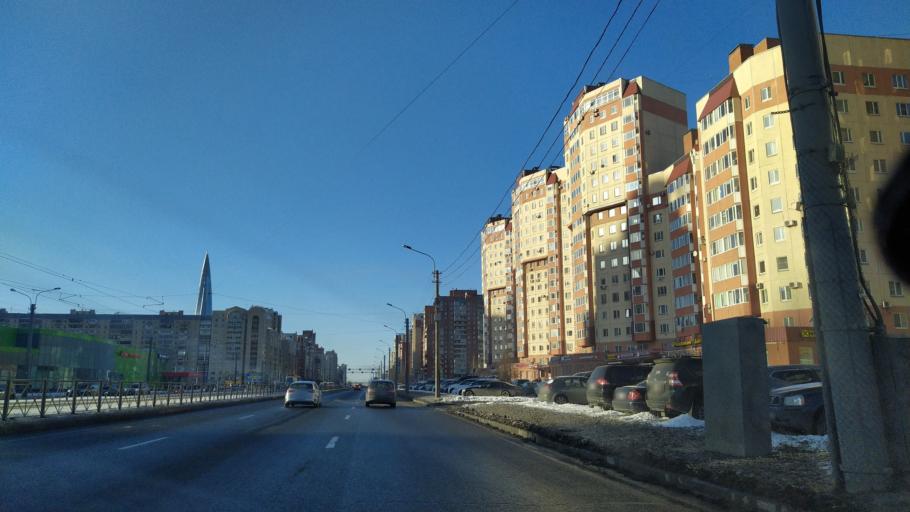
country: RU
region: St.-Petersburg
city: Staraya Derevnya
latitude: 59.9865
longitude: 30.2214
